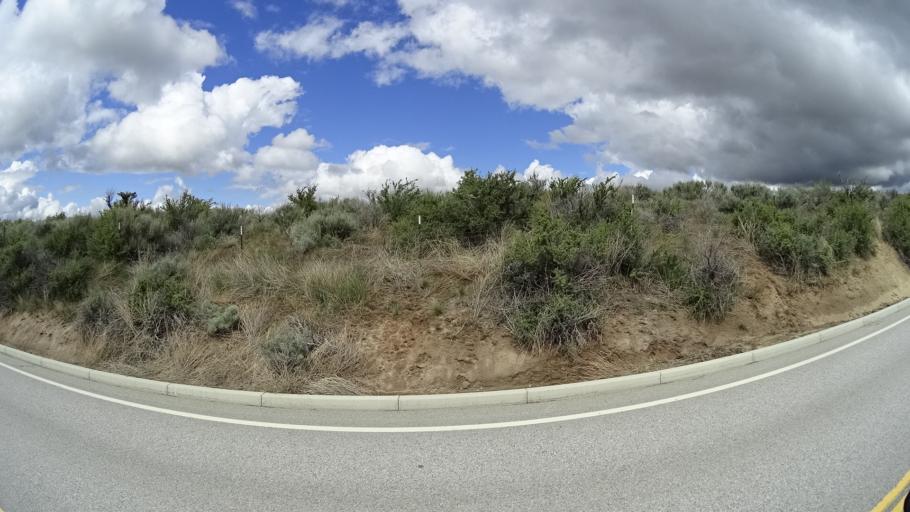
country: US
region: Idaho
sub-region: Ada County
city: Boise
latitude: 43.6951
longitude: -116.1707
